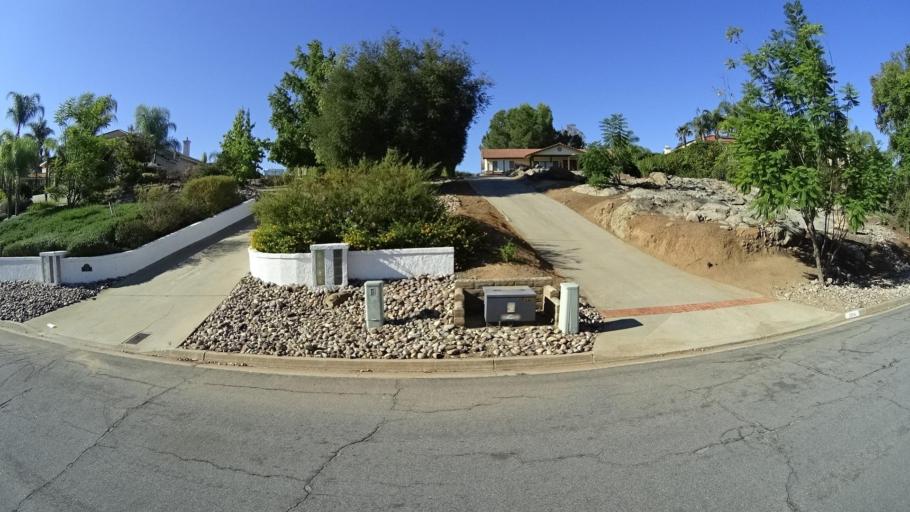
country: US
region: California
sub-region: San Diego County
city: San Diego Country Estates
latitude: 32.9942
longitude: -116.8159
